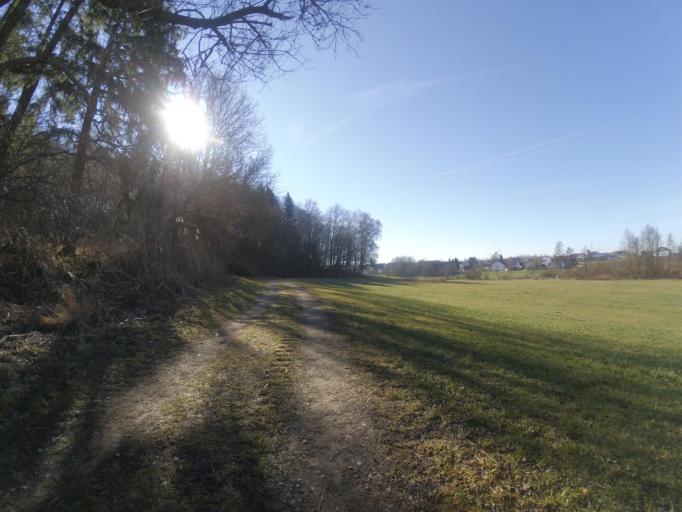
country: DE
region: Baden-Wuerttemberg
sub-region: Tuebingen Region
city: Huttisheim
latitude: 48.2855
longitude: 9.9422
